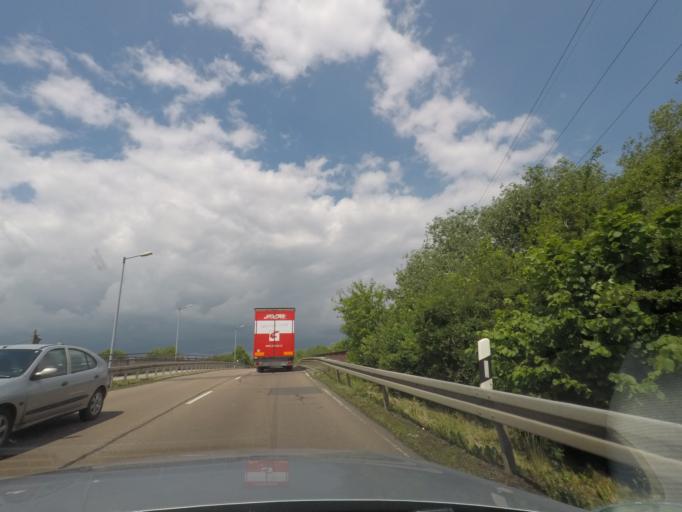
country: DE
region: Saxony
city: Markranstadt
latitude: 51.3122
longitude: 12.2341
